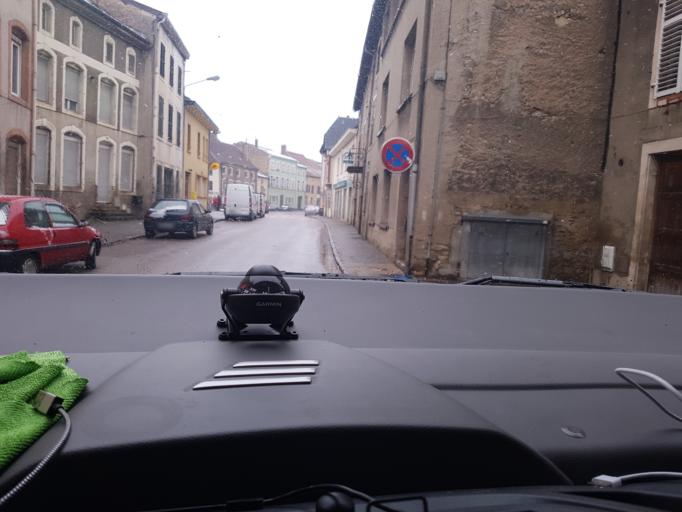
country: FR
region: Lorraine
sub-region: Departement de la Moselle
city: Lorquin
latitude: 48.5890
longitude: 6.8436
